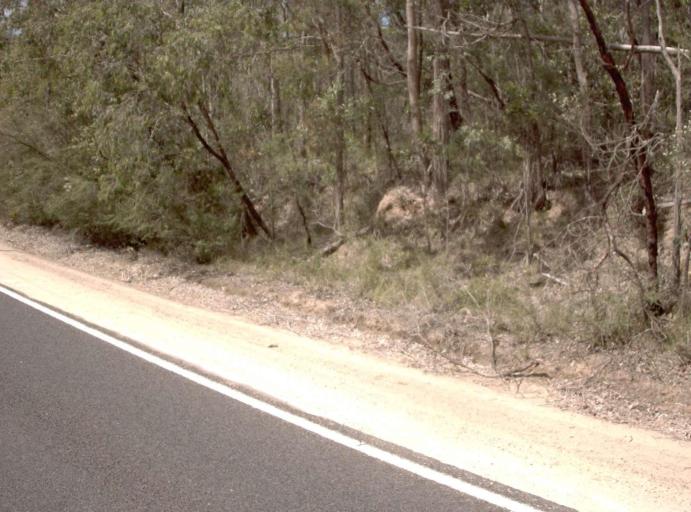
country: AU
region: New South Wales
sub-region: Bega Valley
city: Eden
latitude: -37.4334
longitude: 149.6450
